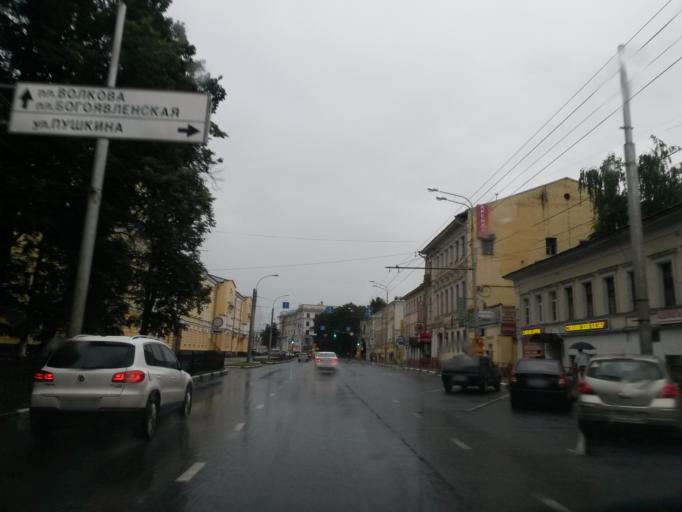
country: RU
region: Jaroslavl
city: Yaroslavl
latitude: 57.6280
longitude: 39.8848
